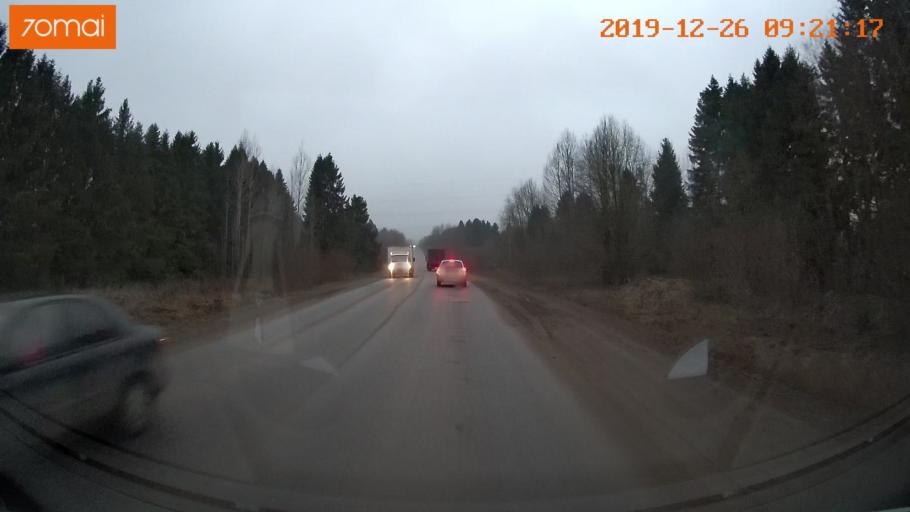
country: RU
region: Vologda
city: Gryazovets
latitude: 58.9692
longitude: 40.2252
